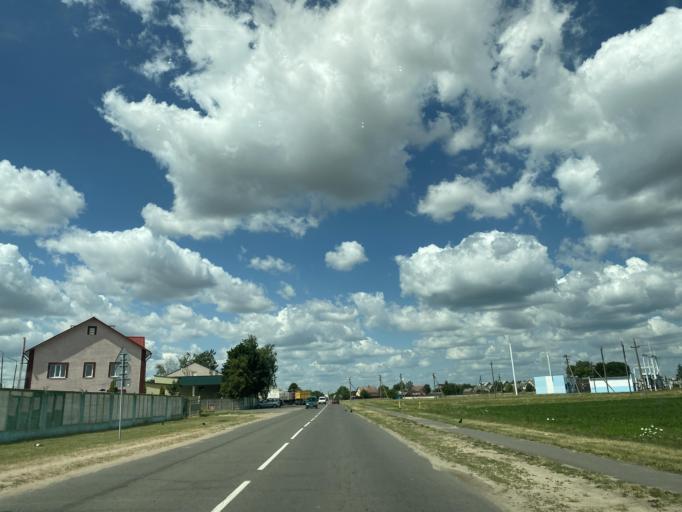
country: BY
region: Brest
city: Ivanava
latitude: 52.1397
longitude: 25.5520
